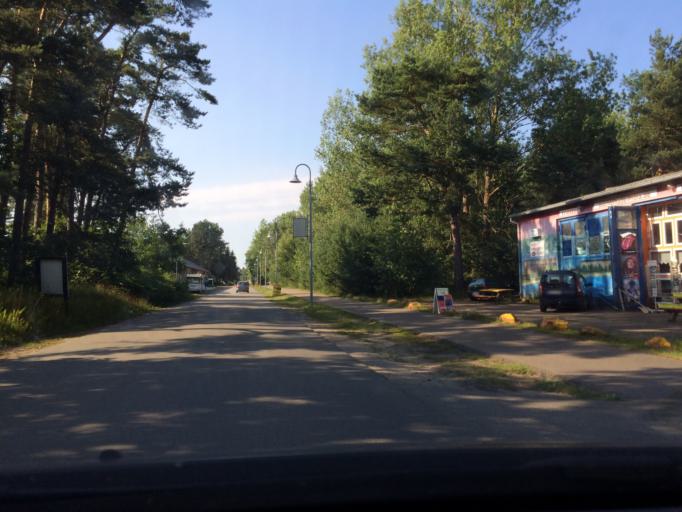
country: DE
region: Mecklenburg-Vorpommern
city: Ostseebad Binz
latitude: 54.4381
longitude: 13.5688
